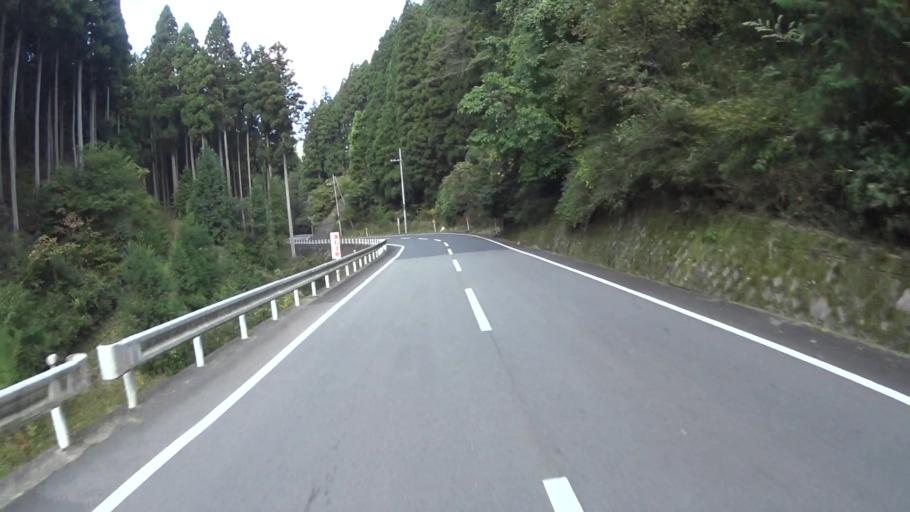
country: JP
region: Kyoto
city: Kameoka
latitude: 35.1225
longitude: 135.5600
